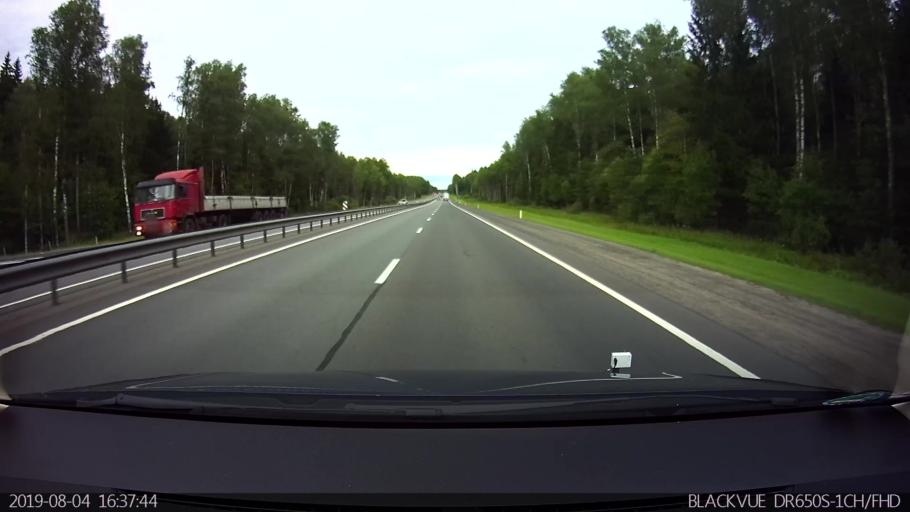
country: RU
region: Smolensk
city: Vyaz'ma
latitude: 55.1958
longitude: 33.8348
